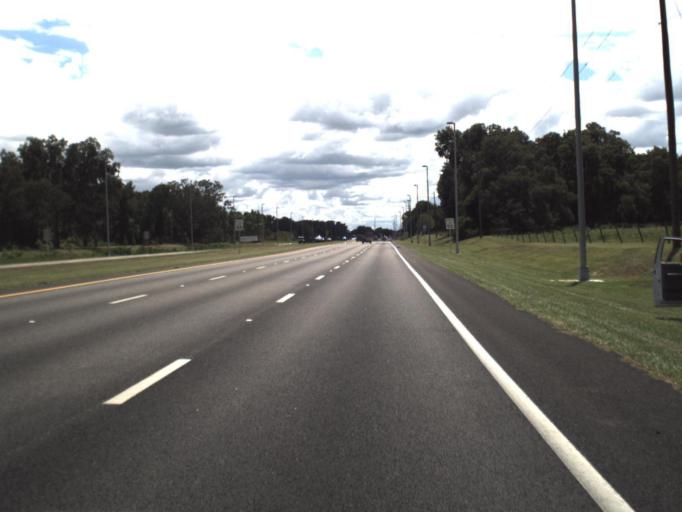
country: US
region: Florida
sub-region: Polk County
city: Bartow
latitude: 27.9214
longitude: -81.8497
